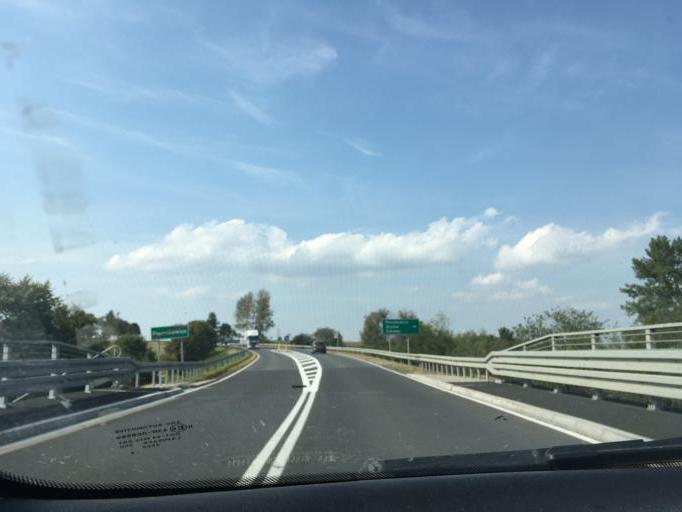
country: PL
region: Opole Voivodeship
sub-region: Powiat prudnicki
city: Laka Prudnicka
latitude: 50.4064
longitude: 17.5095
